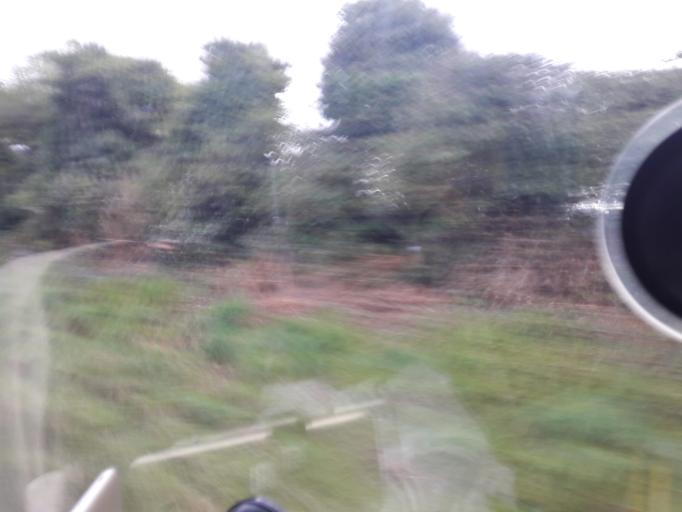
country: IE
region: Leinster
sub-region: An Iarmhi
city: Rathwire
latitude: 53.4880
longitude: -7.1219
